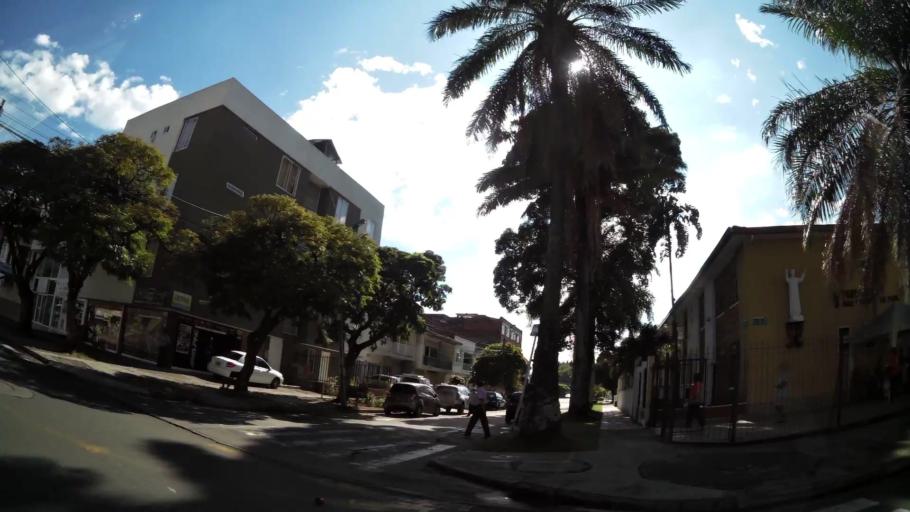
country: CO
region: Valle del Cauca
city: Cali
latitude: 3.4315
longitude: -76.5367
